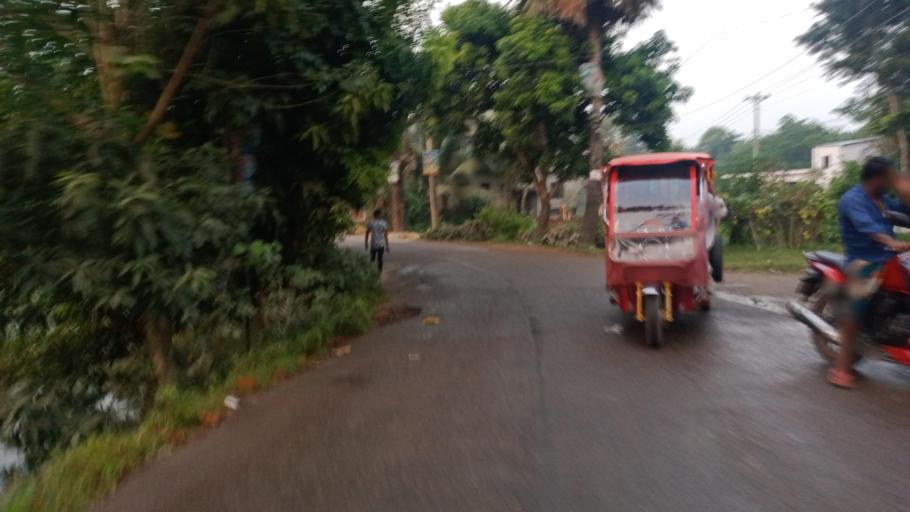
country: BD
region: Chittagong
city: Hajiganj
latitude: 23.3771
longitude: 90.9841
